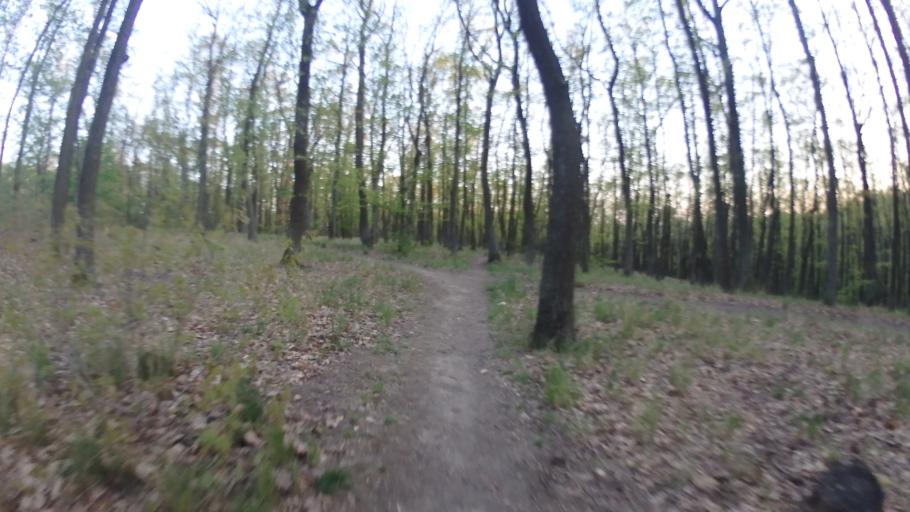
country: CZ
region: South Moravian
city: Troubsko
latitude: 49.1904
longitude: 16.5245
